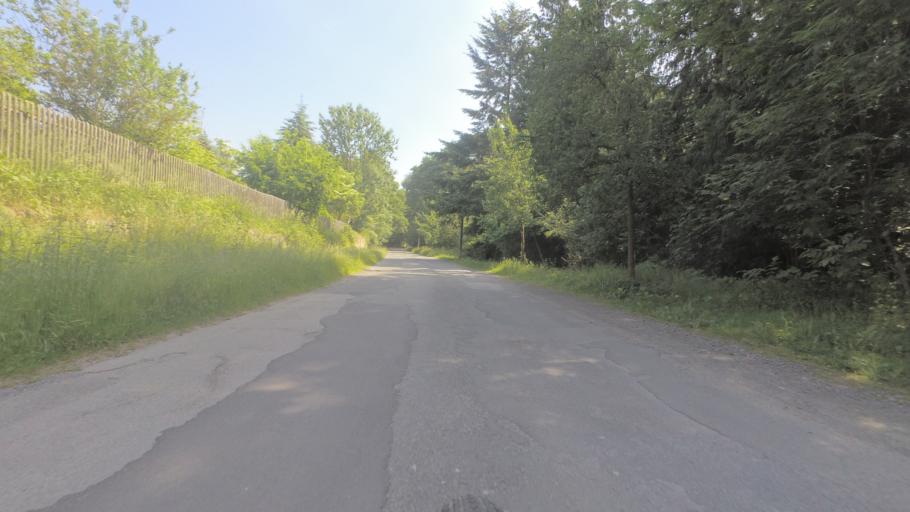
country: DE
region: Saxony-Anhalt
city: Huttenrode
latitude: 51.8057
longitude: 10.9149
